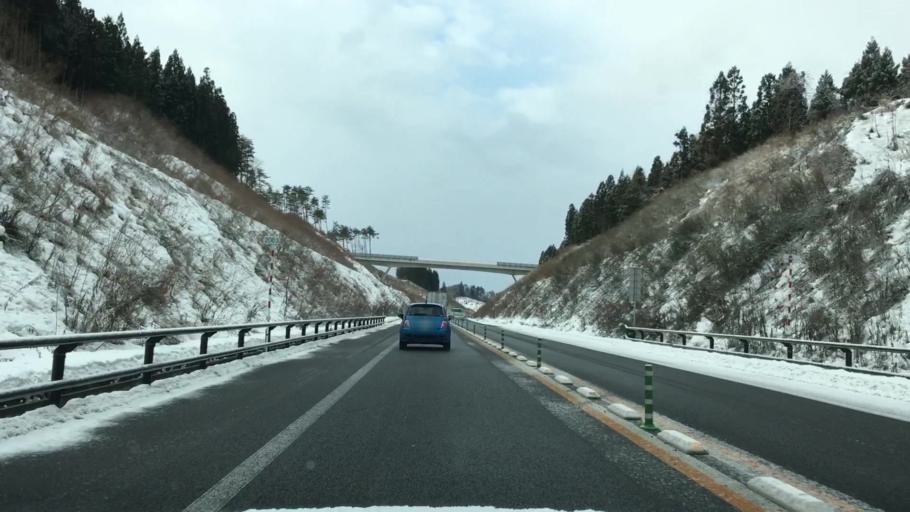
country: JP
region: Akita
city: Takanosu
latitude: 40.2163
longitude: 140.4232
